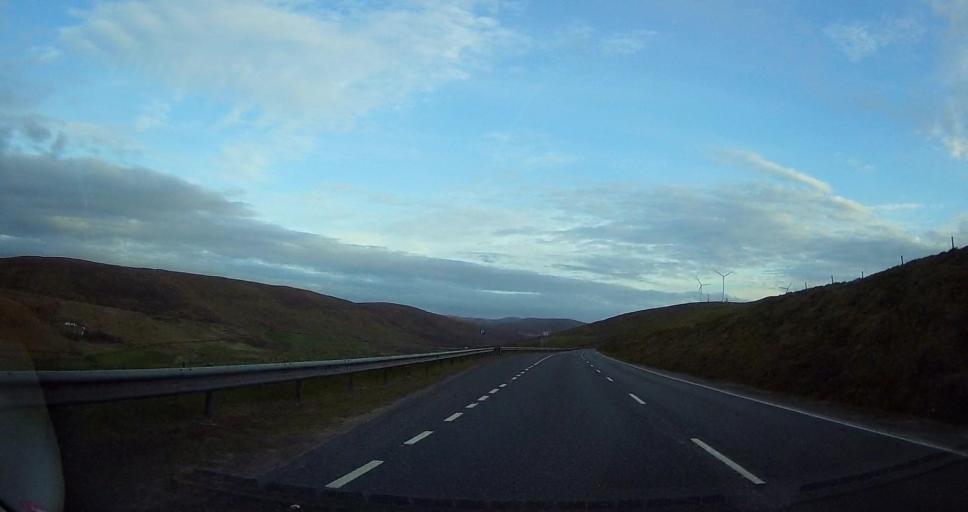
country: GB
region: Scotland
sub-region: Shetland Islands
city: Lerwick
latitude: 60.1731
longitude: -1.2236
